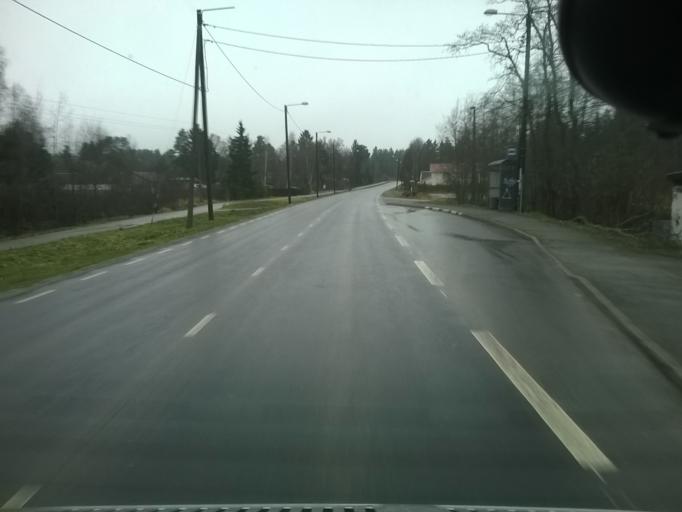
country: EE
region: Harju
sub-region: Saku vald
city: Saku
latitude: 59.2096
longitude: 24.6630
